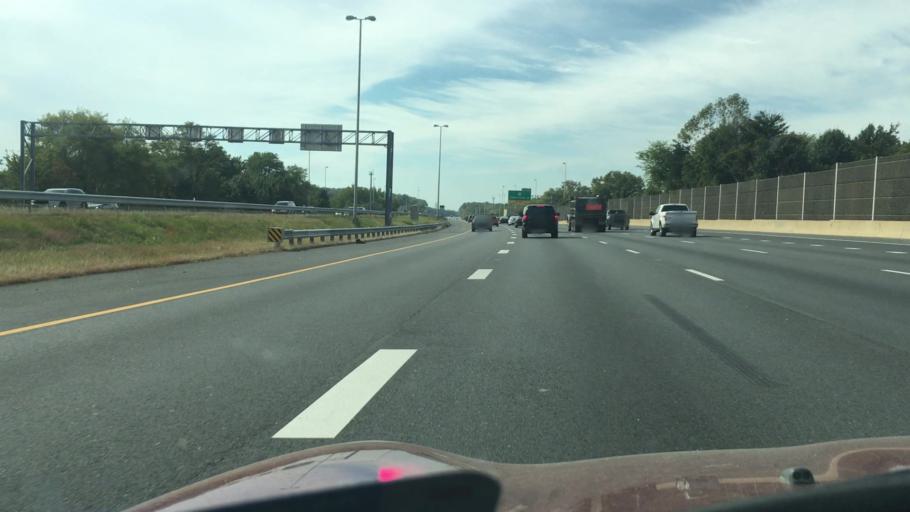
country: US
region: Virginia
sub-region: Fairfax County
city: Centreville
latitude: 38.8417
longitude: -77.4430
